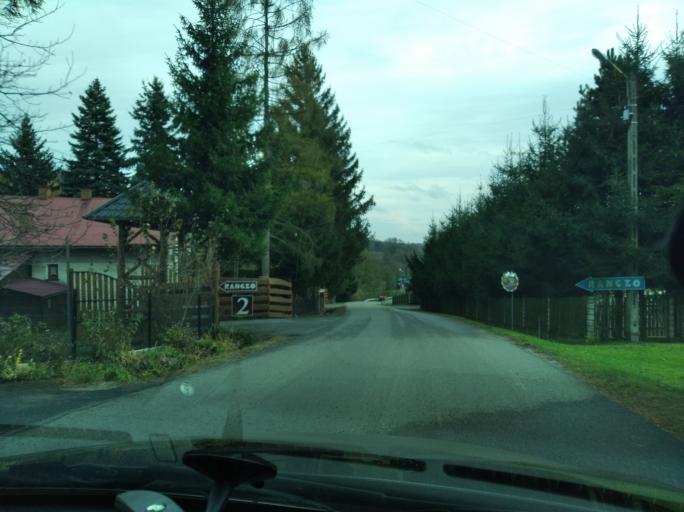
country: PL
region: Subcarpathian Voivodeship
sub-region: Powiat ropczycko-sedziszowski
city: Zagorzyce
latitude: 49.9552
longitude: 21.7193
